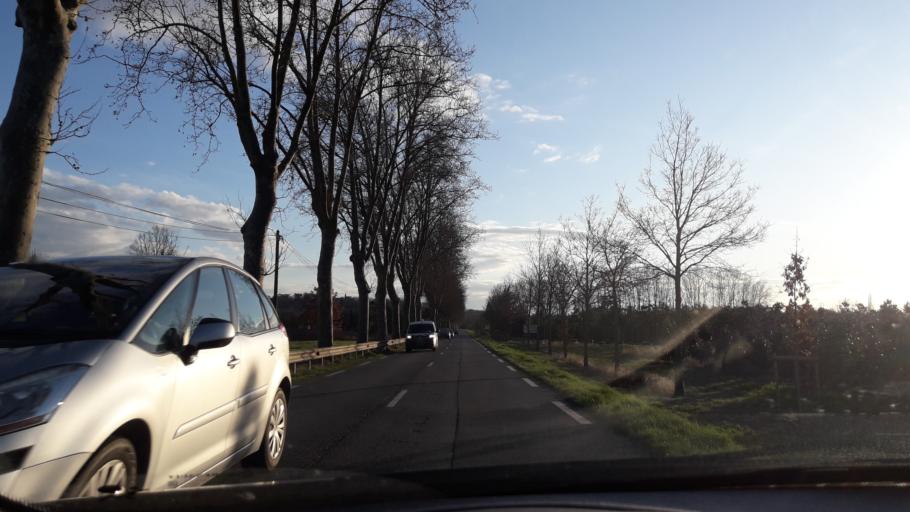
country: FR
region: Midi-Pyrenees
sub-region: Departement de la Haute-Garonne
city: Montaigut-sur-Save
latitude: 43.7042
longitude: 1.2417
